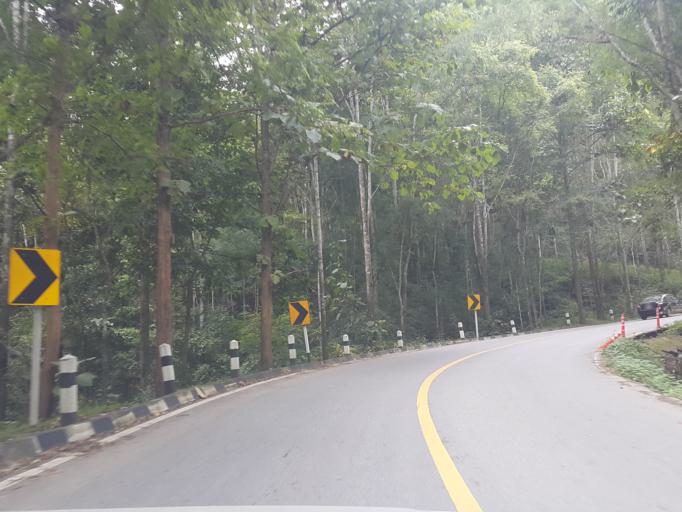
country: TH
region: Mae Hong Son
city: Mae Hi
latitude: 19.2727
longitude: 98.4997
